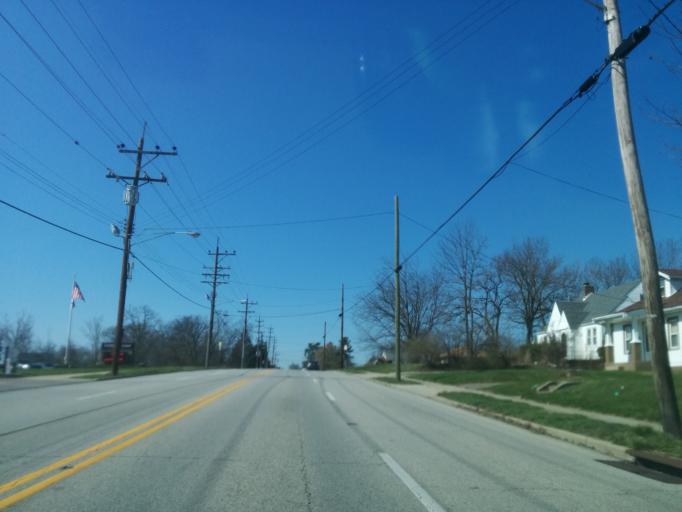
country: US
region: Ohio
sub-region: Hamilton County
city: Monfort Heights
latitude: 39.1897
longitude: -84.5858
